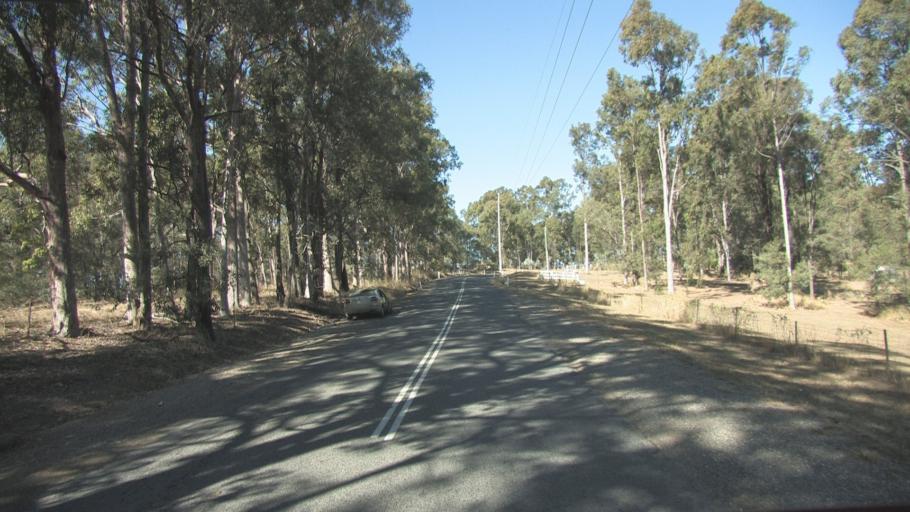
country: AU
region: Queensland
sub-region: Logan
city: Cedar Vale
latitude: -27.8845
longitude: 153.0172
